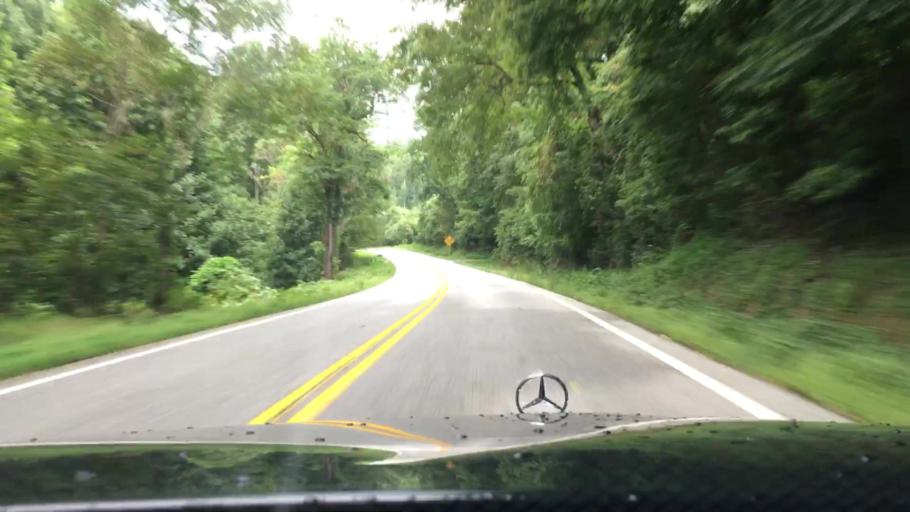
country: US
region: Virginia
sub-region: Nelson County
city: Nellysford
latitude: 37.8307
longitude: -78.9334
